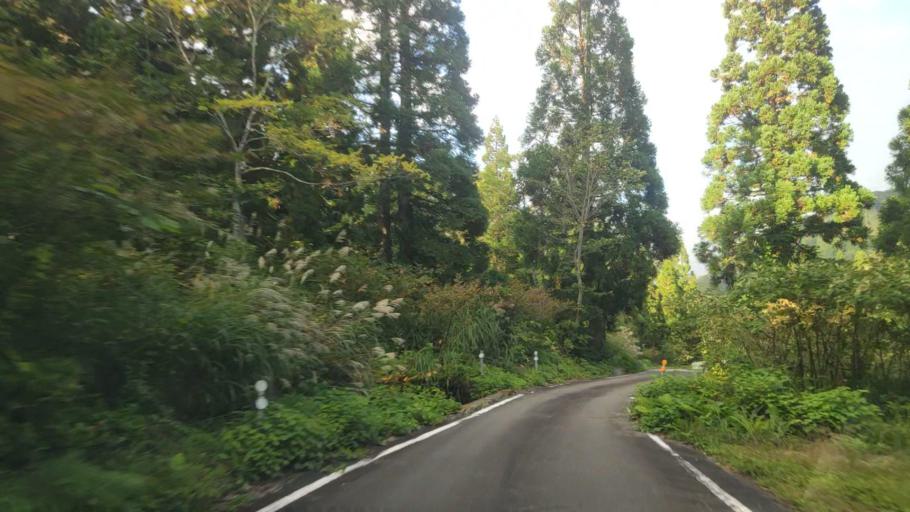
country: JP
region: Toyama
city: Yatsuomachi-higashikumisaka
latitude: 36.3686
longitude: 137.0759
